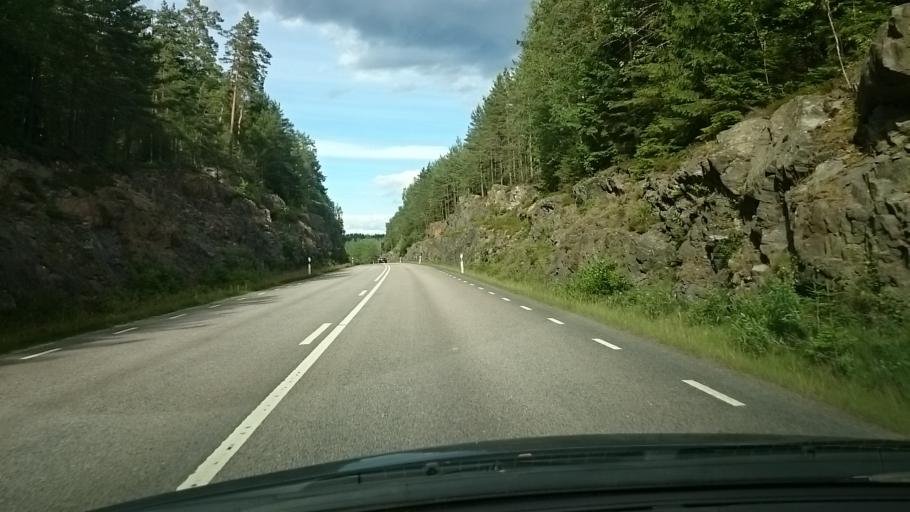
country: SE
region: Vaestra Goetaland
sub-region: Karlsborgs Kommun
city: Karlsborg
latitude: 58.6693
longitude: 14.6276
